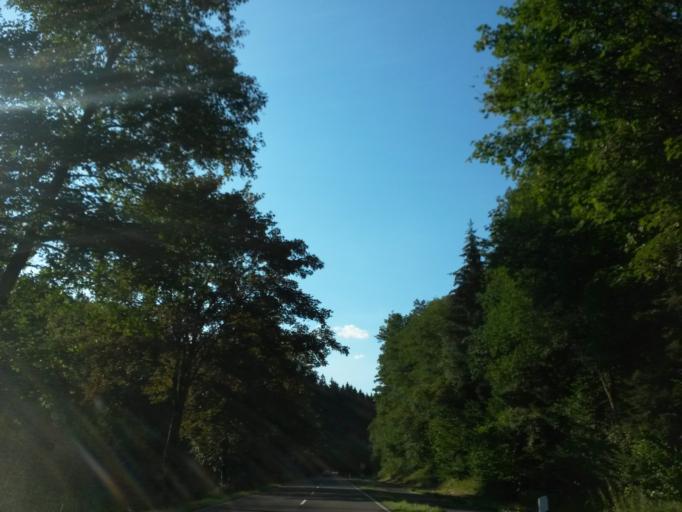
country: DE
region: North Rhine-Westphalia
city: Meinerzhagen
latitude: 51.0700
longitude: 7.6510
